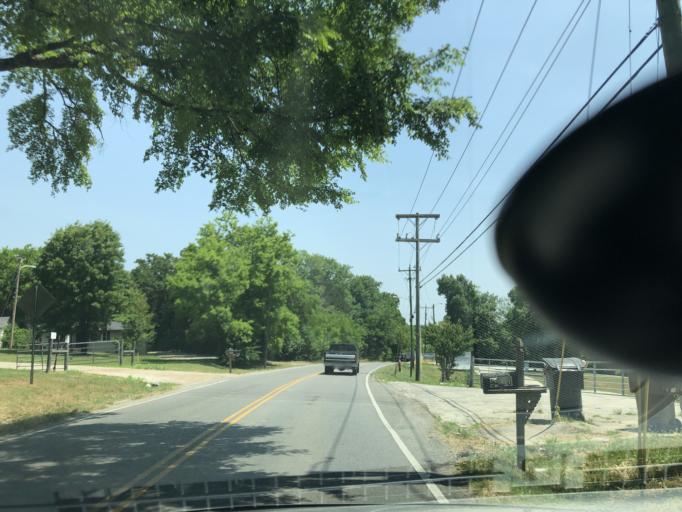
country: US
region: Tennessee
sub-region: Rutherford County
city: La Vergne
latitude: 36.0580
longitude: -86.6172
